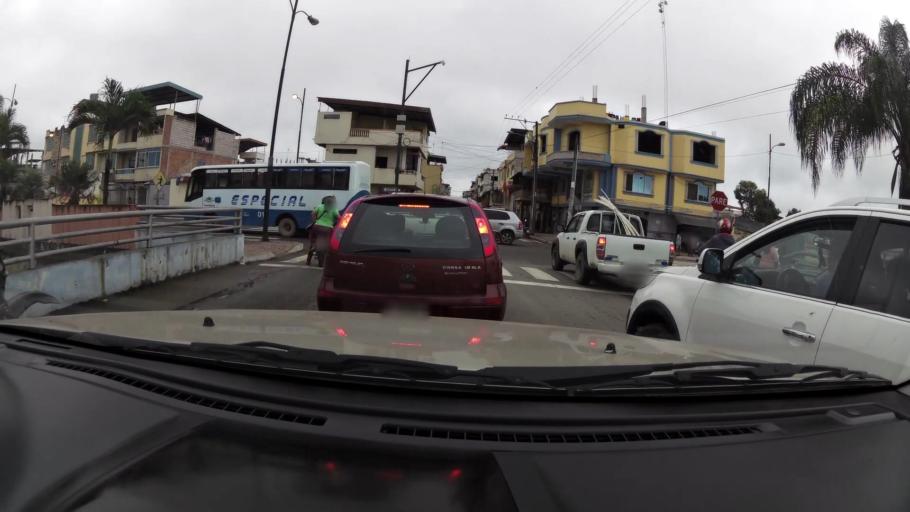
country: EC
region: El Oro
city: Pasaje
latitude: -3.3299
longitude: -79.8048
